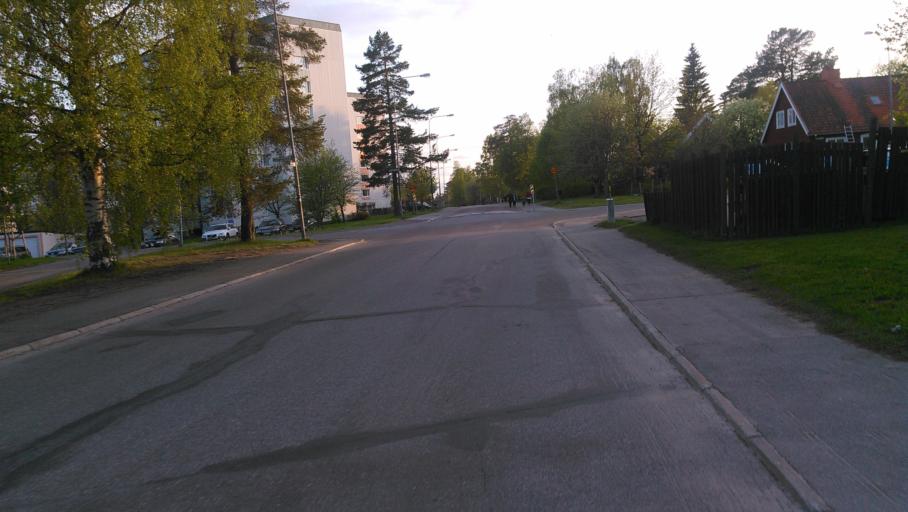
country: SE
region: Vaesterbotten
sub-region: Umea Kommun
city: Umea
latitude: 63.8293
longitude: 20.3047
